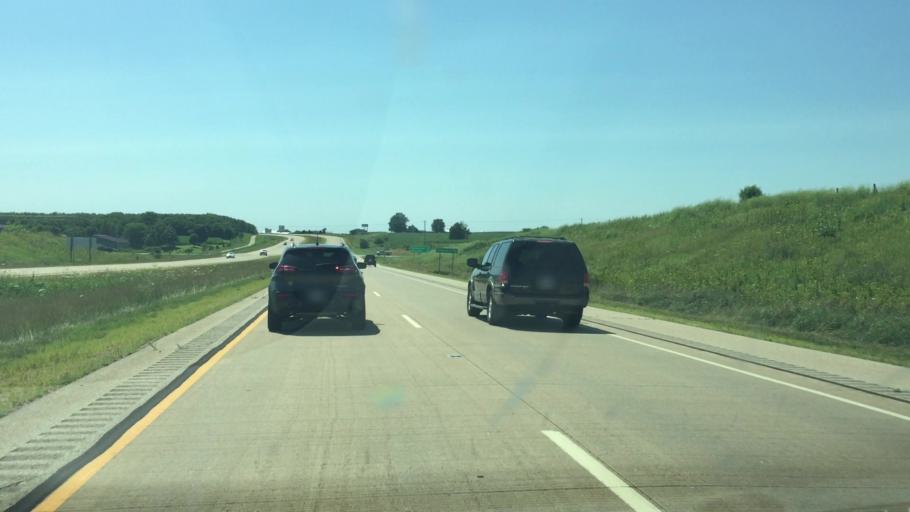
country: US
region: Wisconsin
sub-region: Grant County
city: Platteville
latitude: 42.7113
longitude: -90.5016
